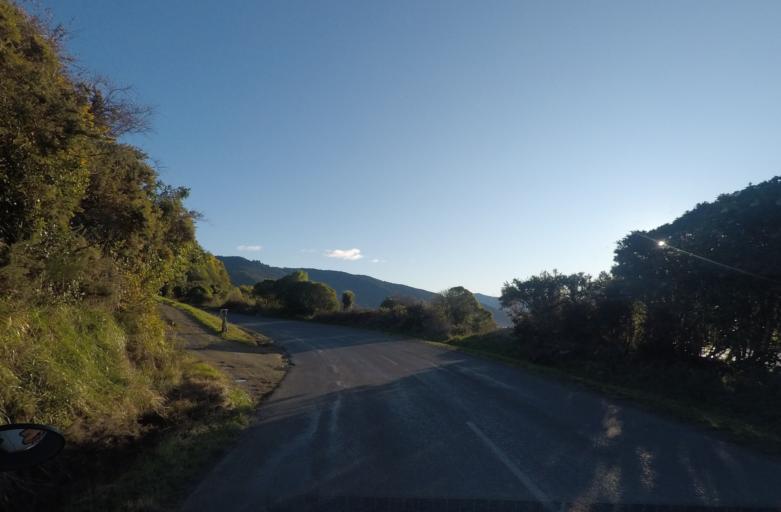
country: NZ
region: Marlborough
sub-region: Marlborough District
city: Picton
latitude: -41.2924
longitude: 173.8416
